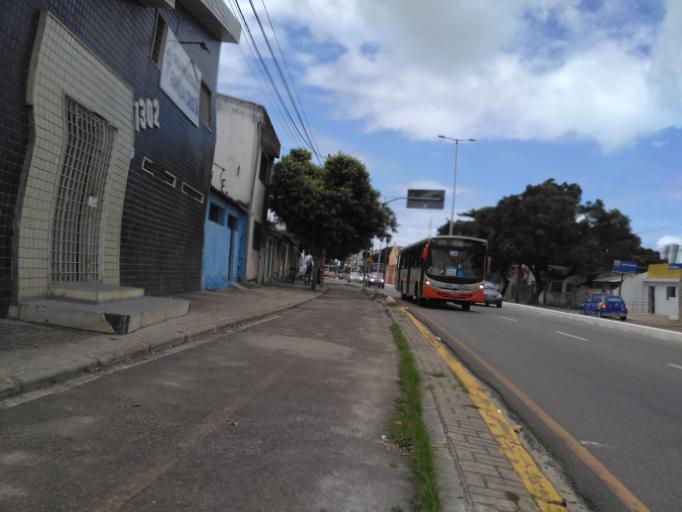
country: BR
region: Pernambuco
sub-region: Recife
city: Recife
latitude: -8.0433
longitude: -34.8837
